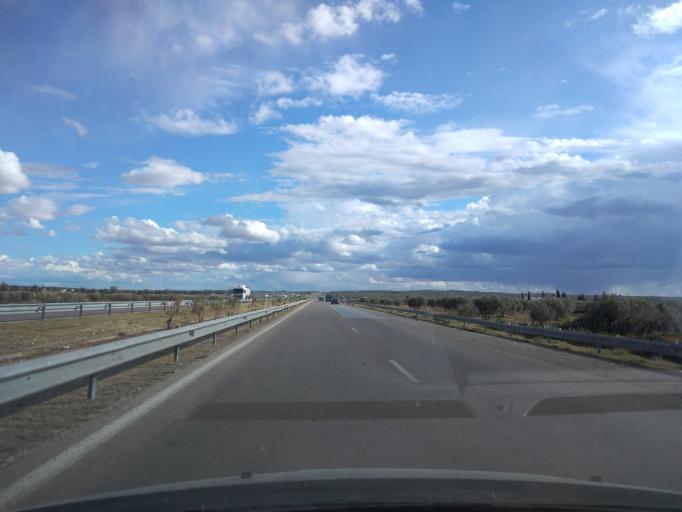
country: TN
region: Al Munastir
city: Manzil Kamil
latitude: 35.5789
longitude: 10.6091
